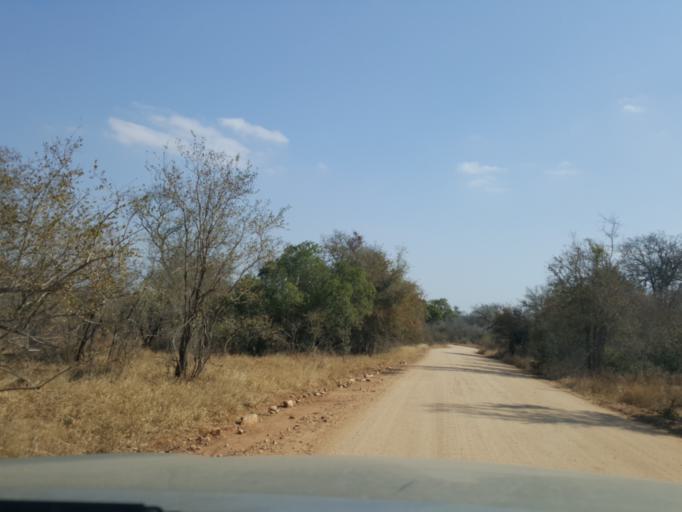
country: ZA
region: Mpumalanga
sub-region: Ehlanzeni District
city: Komatipoort
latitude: -25.2888
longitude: 31.7711
